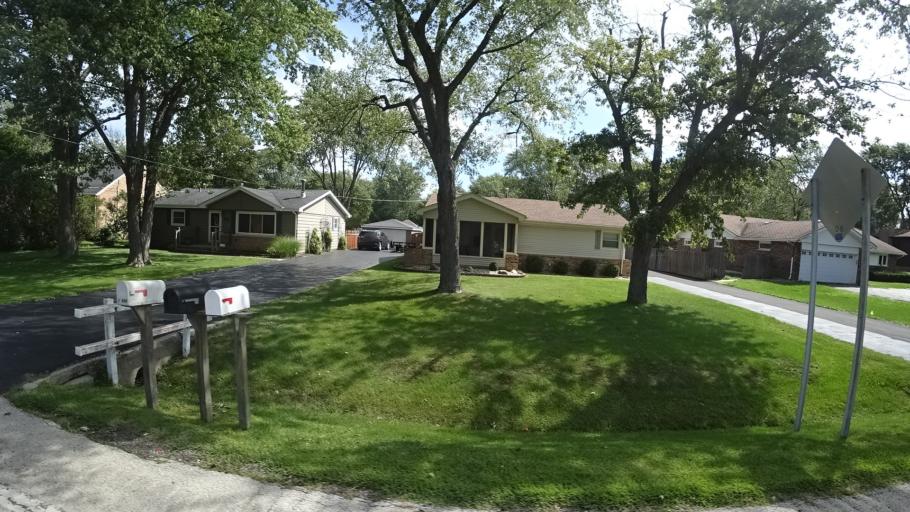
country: US
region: Illinois
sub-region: Cook County
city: Tinley Park
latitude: 41.5712
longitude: -87.7745
